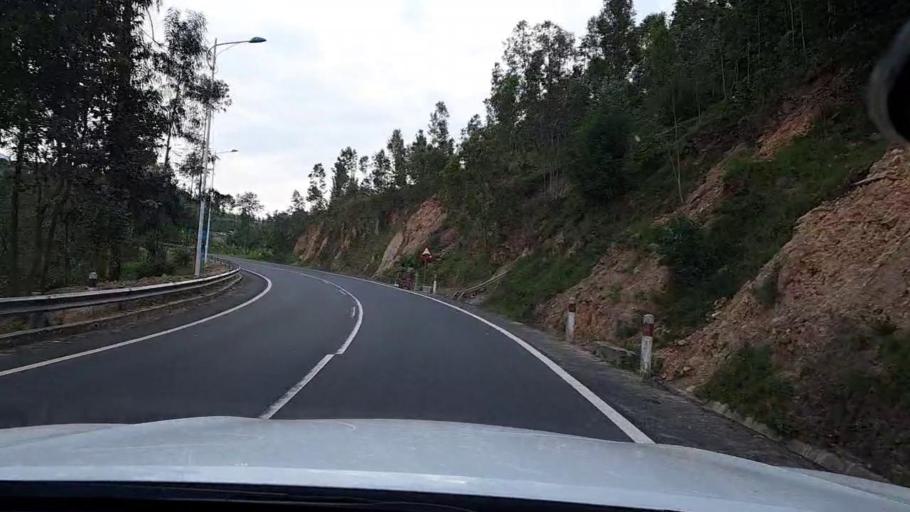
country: RW
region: Western Province
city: Kibuye
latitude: -2.0838
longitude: 29.4156
